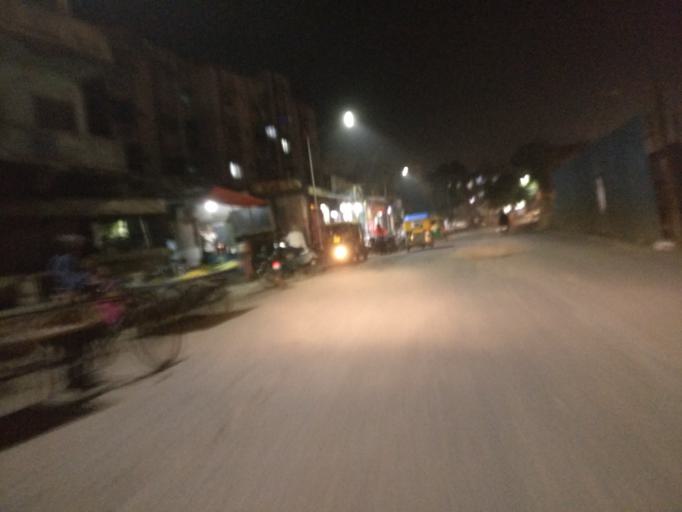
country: IN
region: Gujarat
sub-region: Ahmadabad
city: Ahmedabad
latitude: 23.0025
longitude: 72.5511
